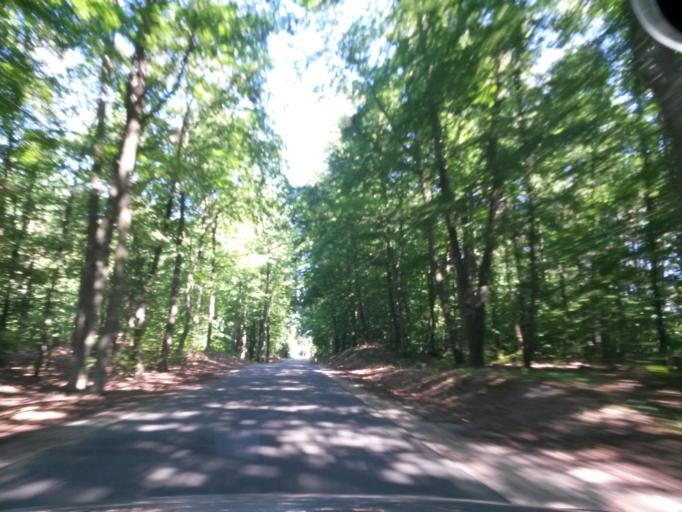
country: DE
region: Brandenburg
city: Lychen
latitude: 53.1415
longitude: 13.3754
